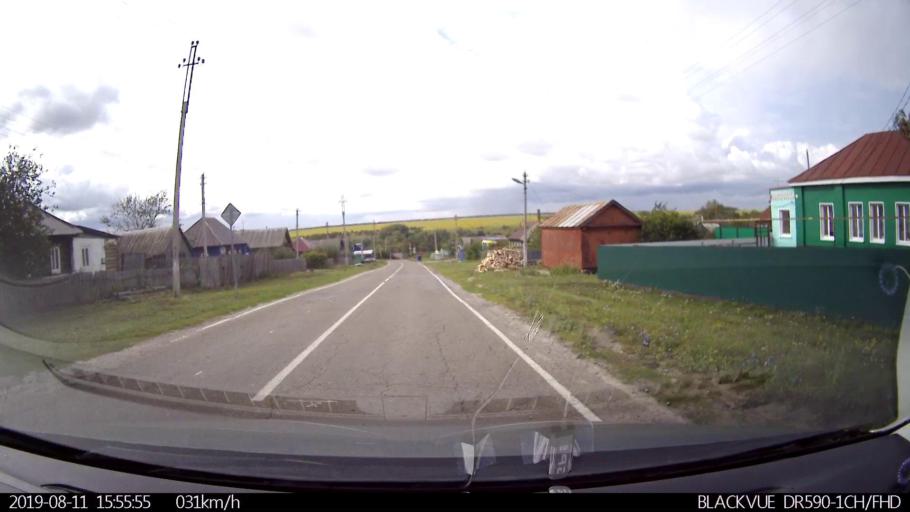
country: RU
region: Ulyanovsk
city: Ignatovka
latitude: 53.9469
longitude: 47.6515
